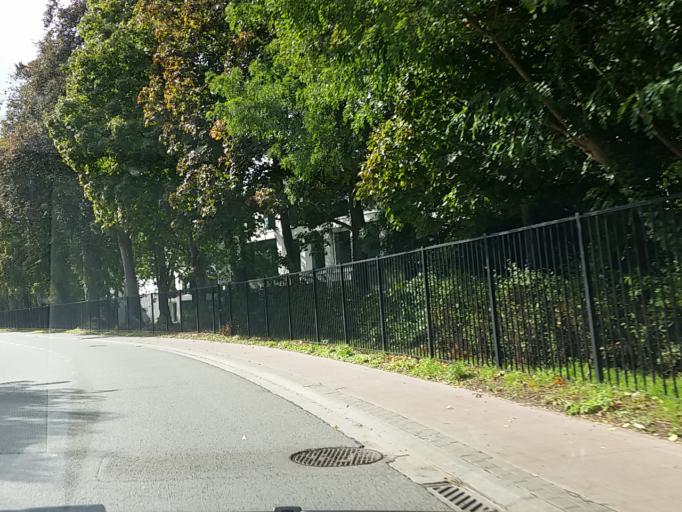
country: BE
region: Flanders
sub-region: Provincie Vlaams-Brabant
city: Machelen
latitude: 50.9210
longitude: 4.4512
